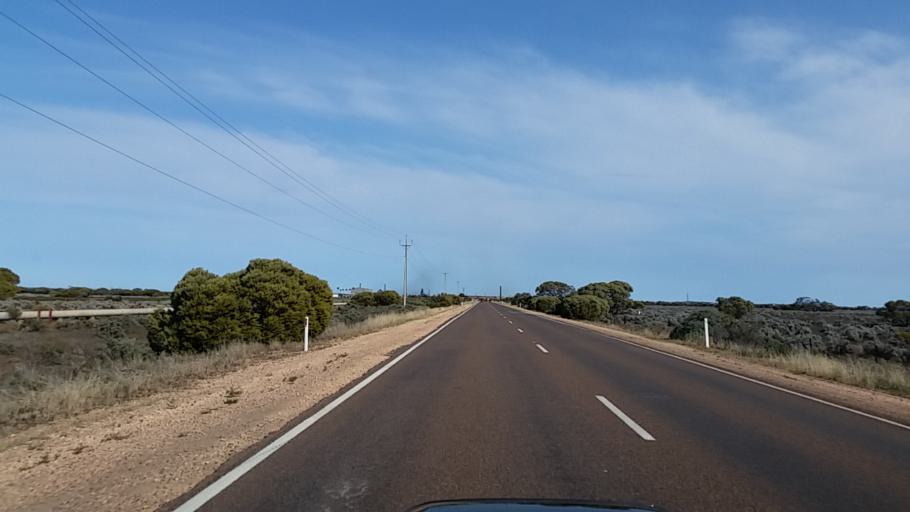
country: AU
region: South Australia
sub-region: Whyalla
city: Whyalla
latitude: -32.9716
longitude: 137.5793
